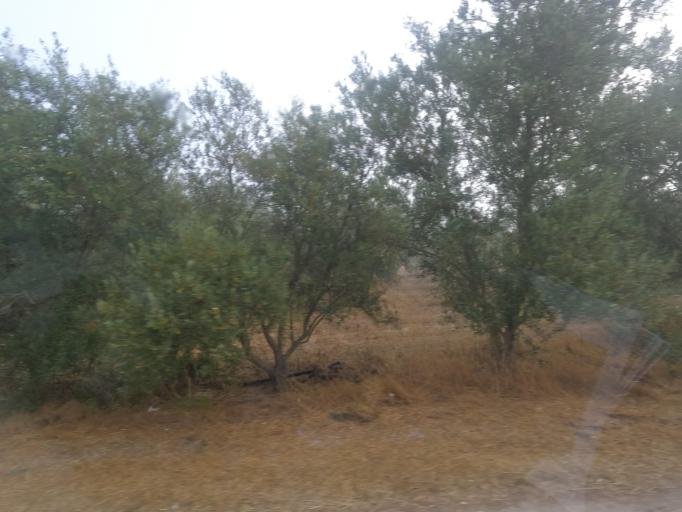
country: CY
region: Ammochostos
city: Acheritou
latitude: 35.0915
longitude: 33.8803
